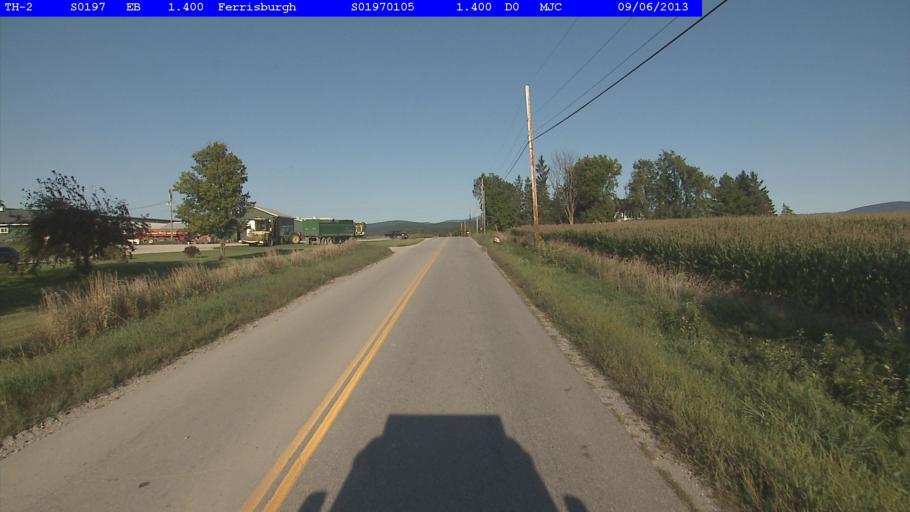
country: US
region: Vermont
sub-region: Addison County
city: Vergennes
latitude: 44.1750
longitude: -73.2117
